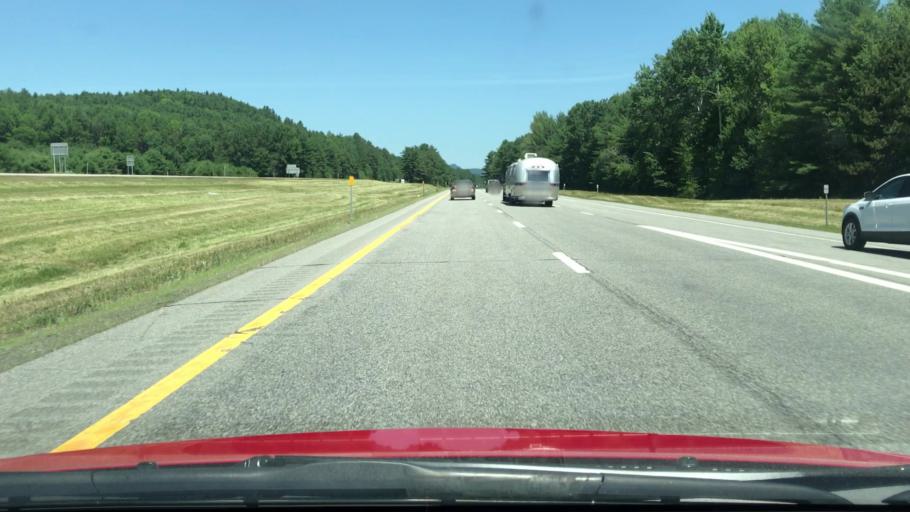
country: US
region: New York
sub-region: Essex County
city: Elizabethtown
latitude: 44.2882
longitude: -73.5317
